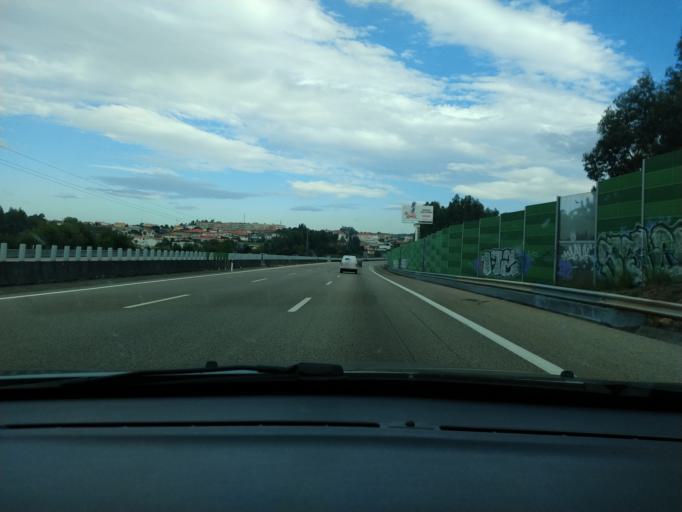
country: PT
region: Aveiro
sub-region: Santa Maria da Feira
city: Rio Meao
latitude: 40.9510
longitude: -8.5725
